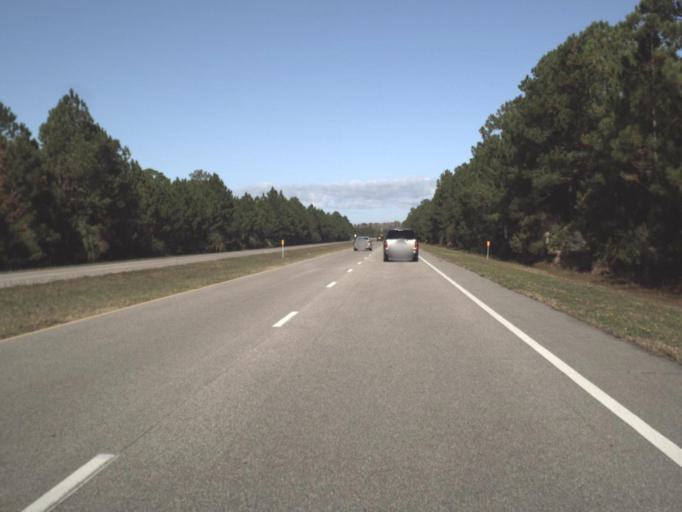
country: US
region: Florida
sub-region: Volusia County
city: Holly Hill
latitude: 29.2185
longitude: -81.0815
